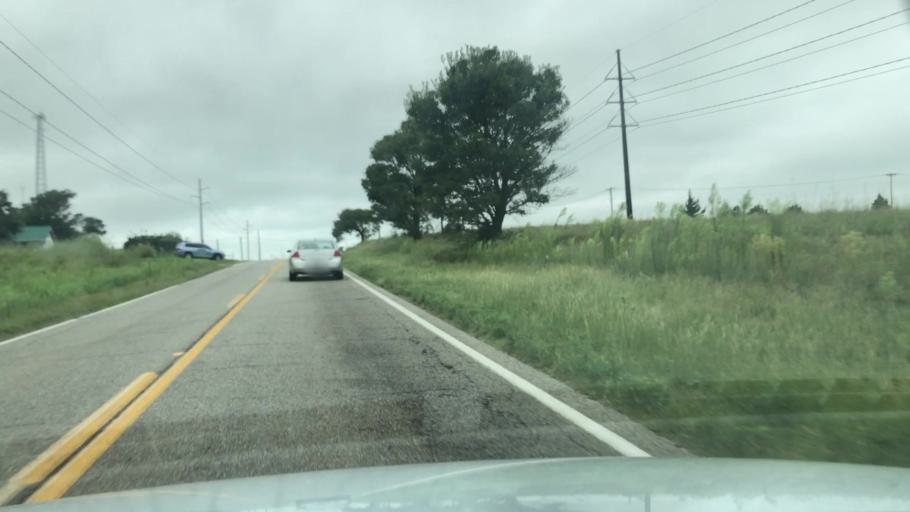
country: US
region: Oklahoma
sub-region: Washington County
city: Dewey
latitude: 36.7280
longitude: -95.8890
